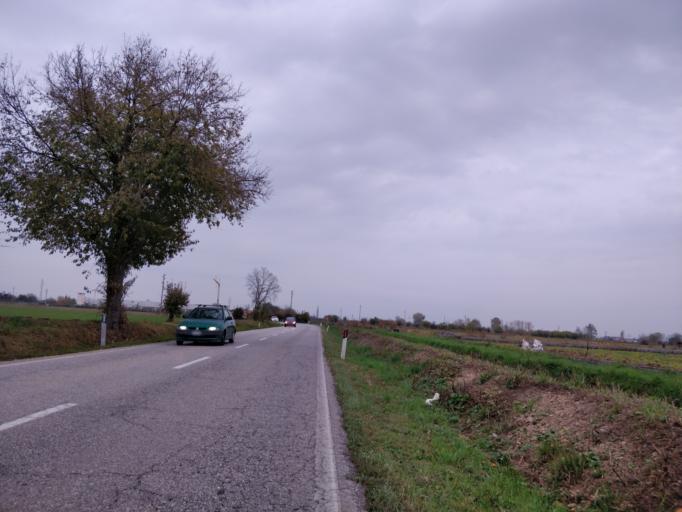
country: IT
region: Friuli Venezia Giulia
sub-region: Provincia di Udine
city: Talmassons
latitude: 45.9327
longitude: 13.1278
